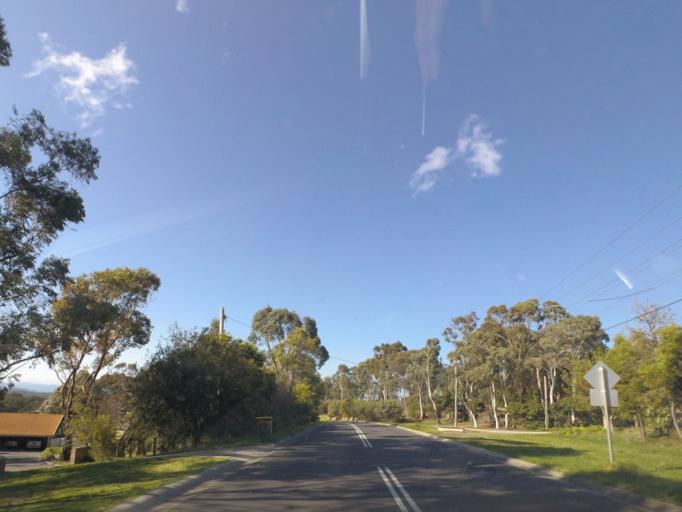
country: AU
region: Victoria
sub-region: Manningham
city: Park Orchards
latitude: -37.7712
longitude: 145.2189
